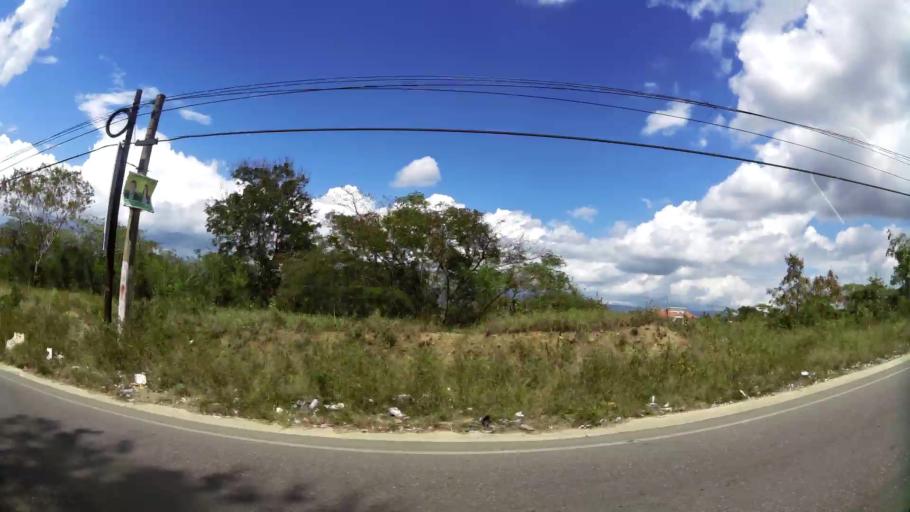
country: DO
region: Santiago
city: Santiago de los Caballeros
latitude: 19.4194
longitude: -70.6809
